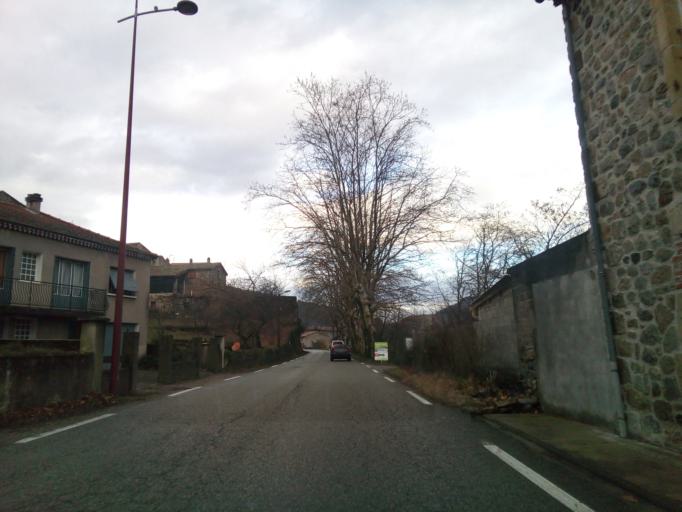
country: FR
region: Rhone-Alpes
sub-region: Departement de l'Ardeche
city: Saint-Sauveur-de-Montagut
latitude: 44.8060
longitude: 4.6243
